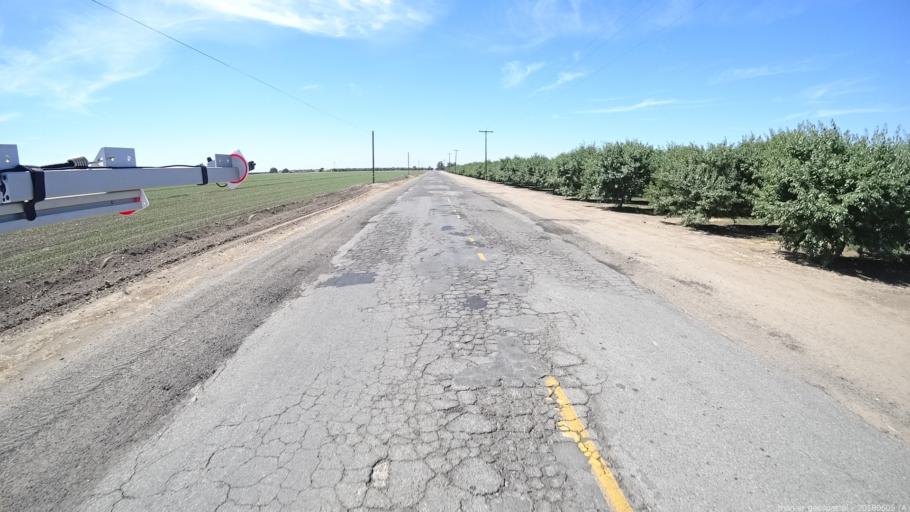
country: US
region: California
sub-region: Madera County
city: Chowchilla
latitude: 37.1230
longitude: -120.3828
